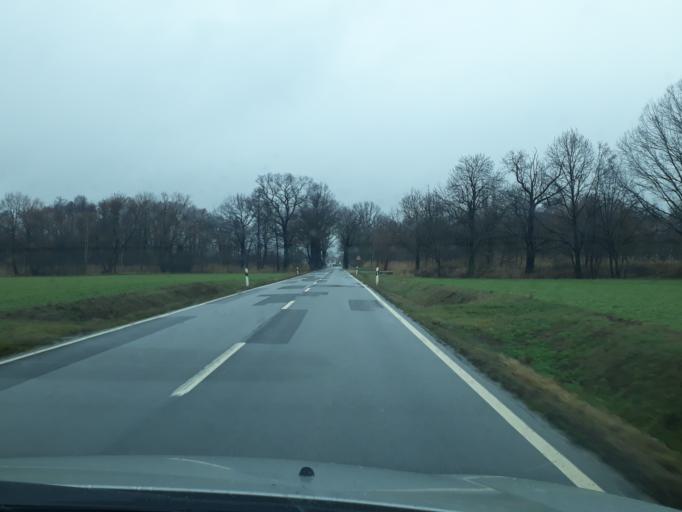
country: DE
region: Saxony
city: Malschwitz
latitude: 51.2317
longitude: 14.5134
